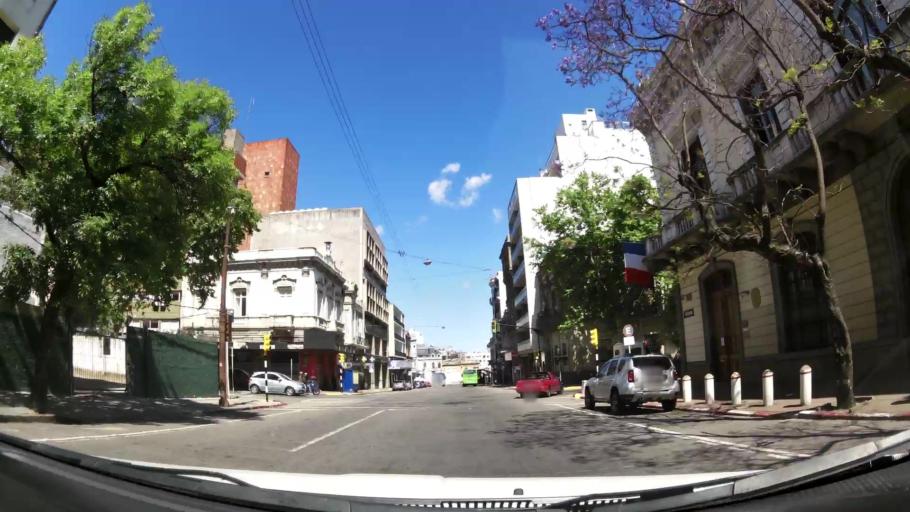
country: UY
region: Montevideo
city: Montevideo
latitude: -34.9037
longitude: -56.1983
